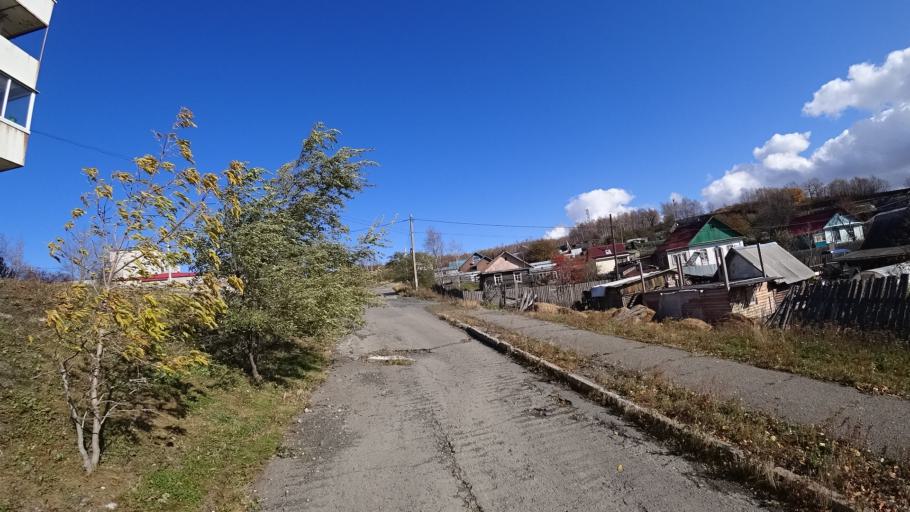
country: RU
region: Khabarovsk Krai
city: Amursk
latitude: 50.2398
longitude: 136.9183
